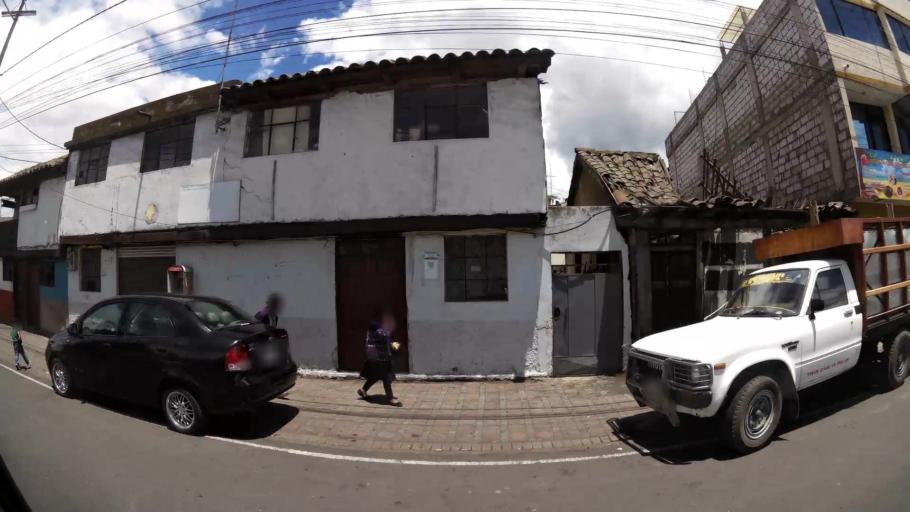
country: EC
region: Tungurahua
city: Pelileo
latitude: -1.3276
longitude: -78.5417
